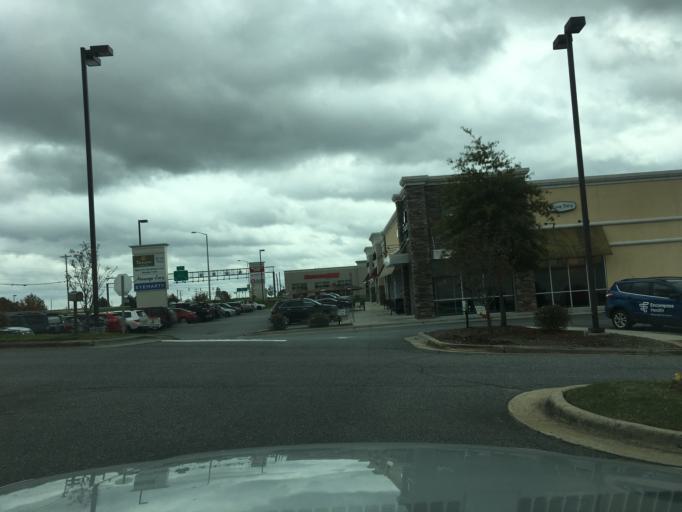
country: US
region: North Carolina
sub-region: Catawba County
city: Hickory
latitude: 35.7030
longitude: -81.2970
